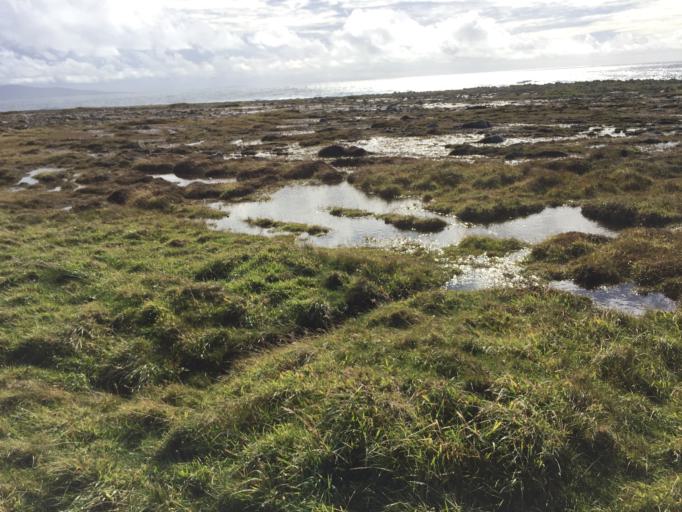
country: IE
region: Ulster
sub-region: County Donegal
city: Derrybeg
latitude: 55.2701
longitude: -8.2480
